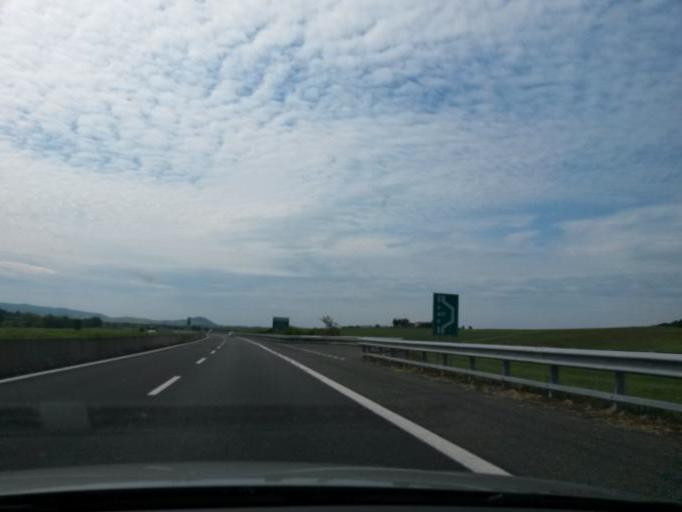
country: IT
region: Tuscany
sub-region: Province of Pisa
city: Orciano Pisano
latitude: 43.4803
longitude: 10.4859
